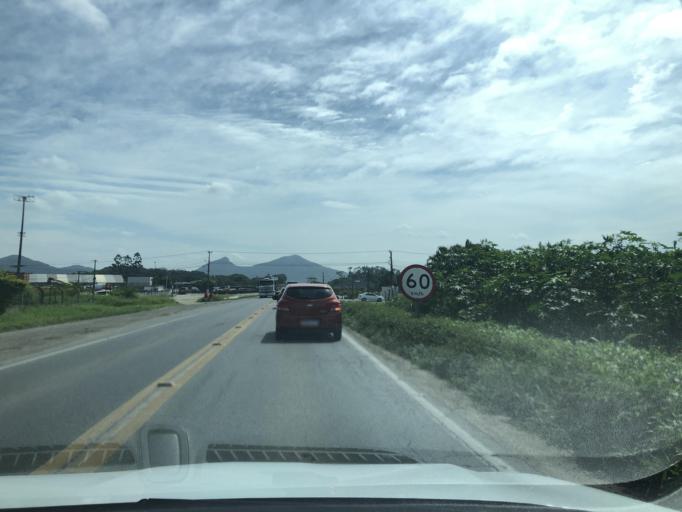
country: BR
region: Santa Catarina
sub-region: Sao Francisco Do Sul
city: Sao Francisco do Sul
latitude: -26.2622
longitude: -48.6285
